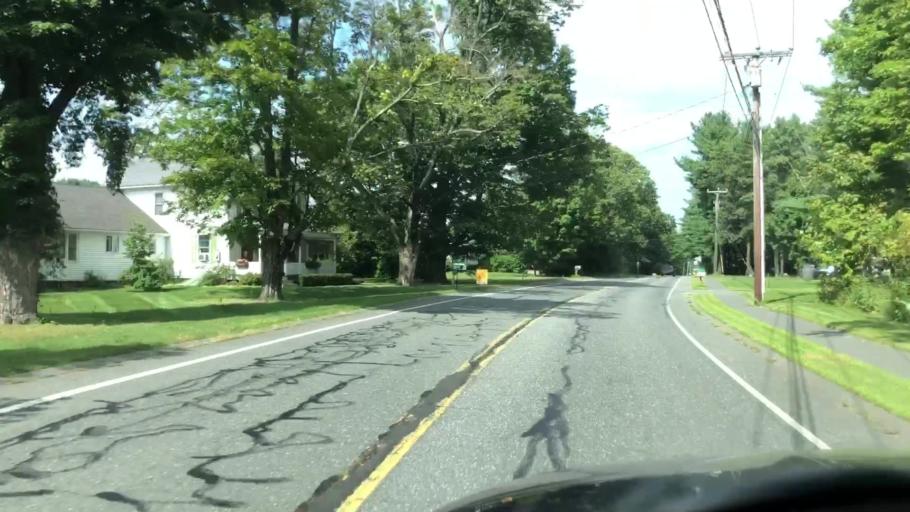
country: US
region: Massachusetts
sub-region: Hampshire County
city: Southampton
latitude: 42.2444
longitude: -72.7258
